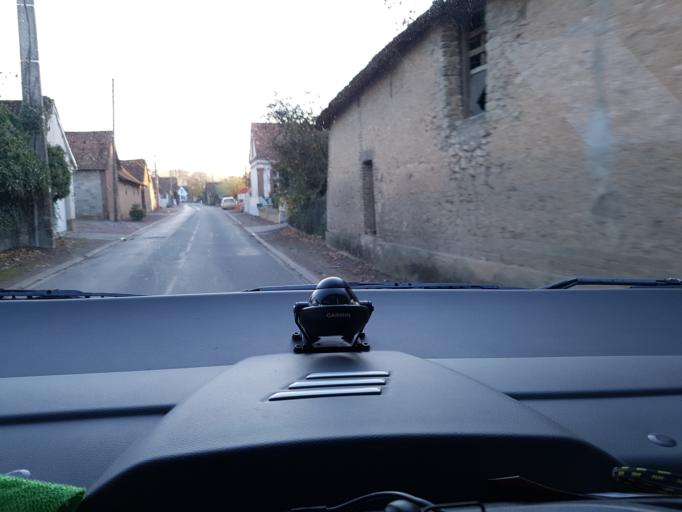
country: FR
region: Nord-Pas-de-Calais
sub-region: Departement du Pas-de-Calais
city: Beaurainville
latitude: 50.4765
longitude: 1.8582
